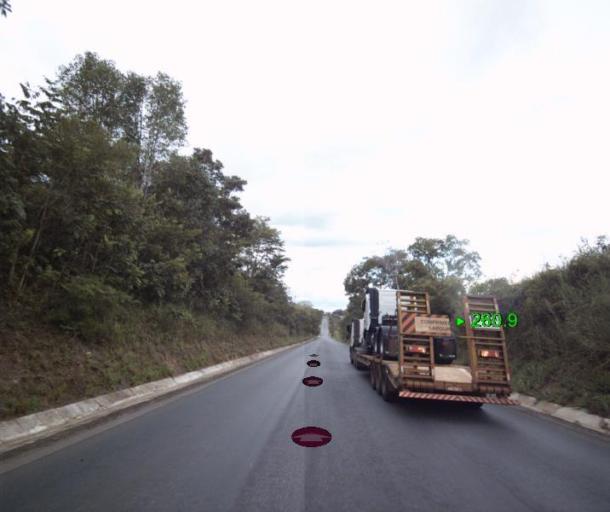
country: BR
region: Goias
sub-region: Itapaci
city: Itapaci
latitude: -15.0045
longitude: -49.4140
